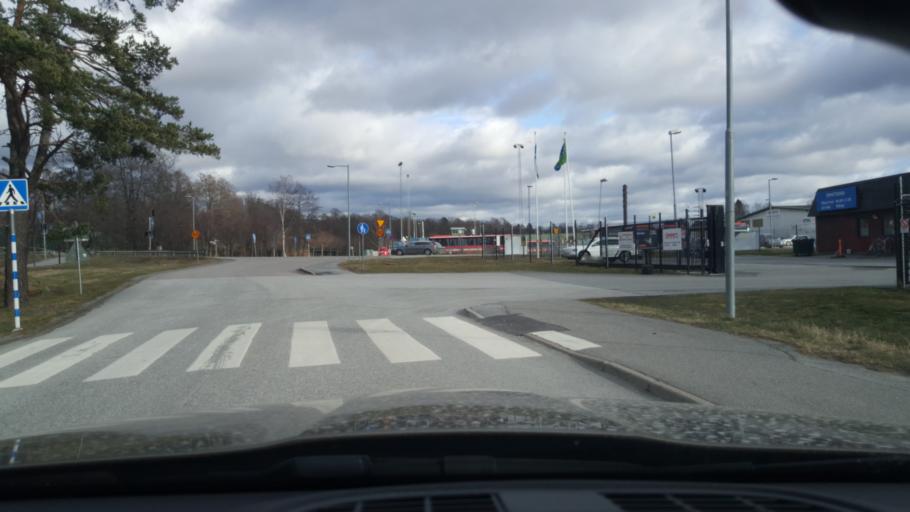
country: SE
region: Stockholm
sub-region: Osterakers Kommun
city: Akersberga
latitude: 59.4935
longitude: 18.2760
